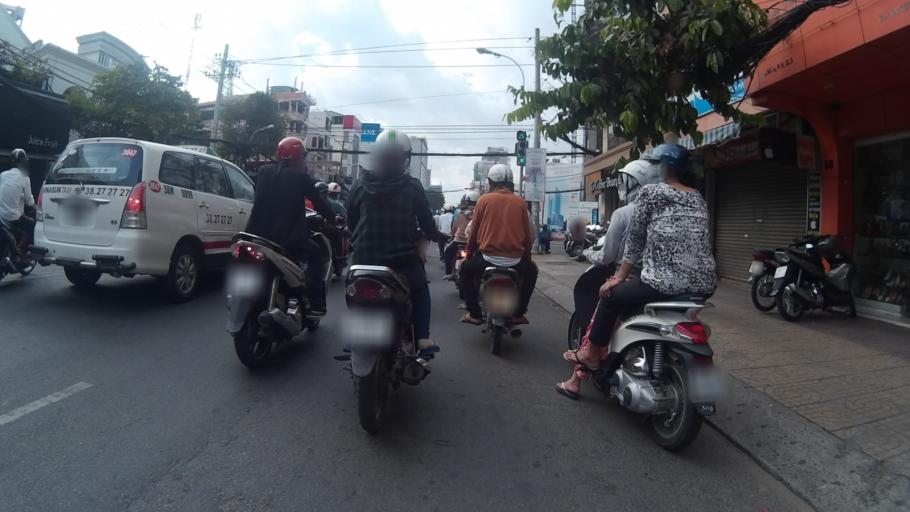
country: VN
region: Ho Chi Minh City
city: Quan Ba
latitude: 10.7742
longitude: 106.6886
